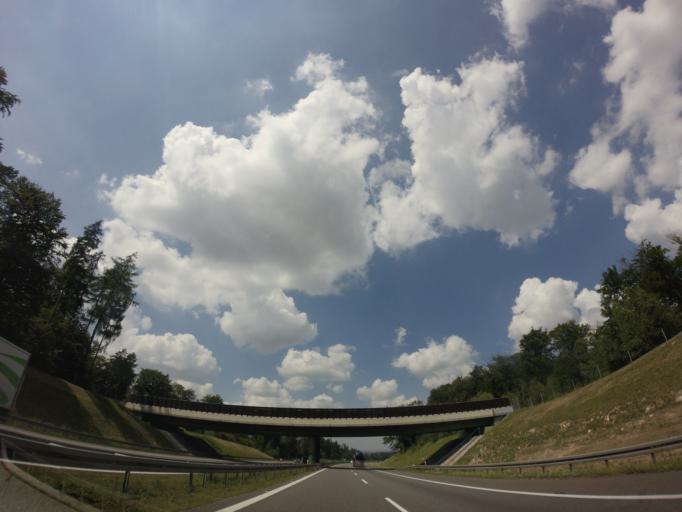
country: PL
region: Opole Voivodeship
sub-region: Powiat krapkowicki
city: Zdzieszowice
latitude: 50.4704
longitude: 18.1439
